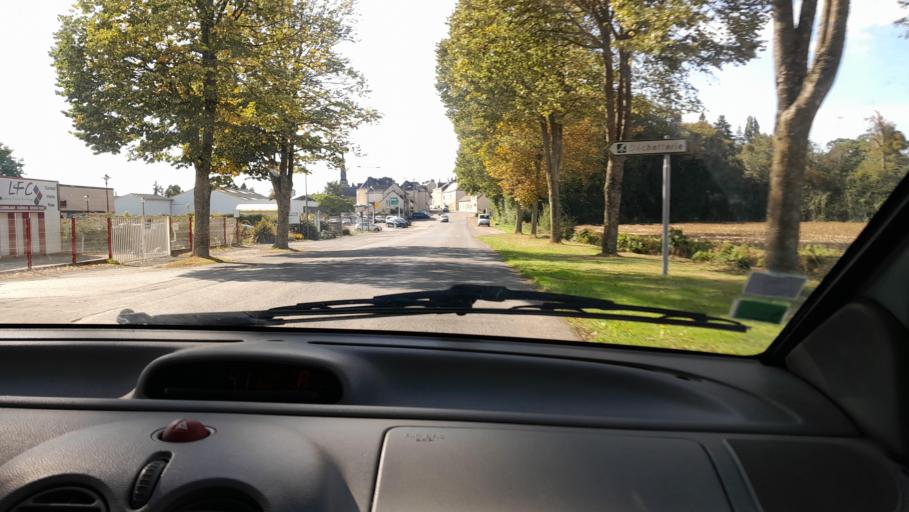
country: FR
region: Brittany
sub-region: Departement d'Ille-et-Vilaine
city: Argentre-du-Plessis
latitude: 47.9705
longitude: -1.1135
